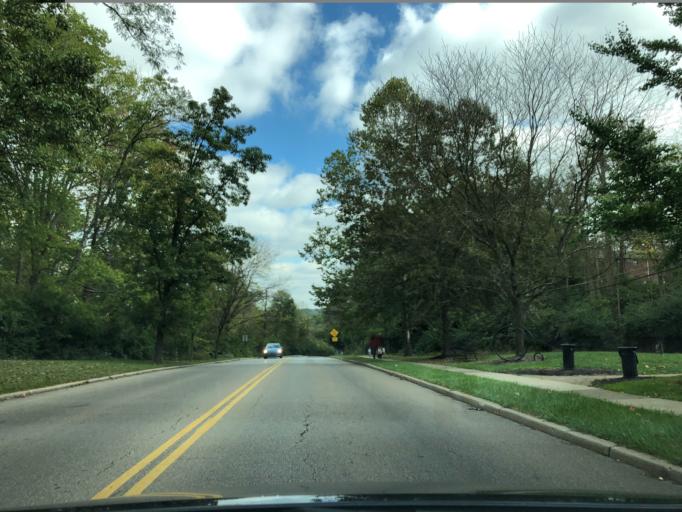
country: US
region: Ohio
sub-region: Hamilton County
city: Loveland
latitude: 39.2702
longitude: -84.2699
